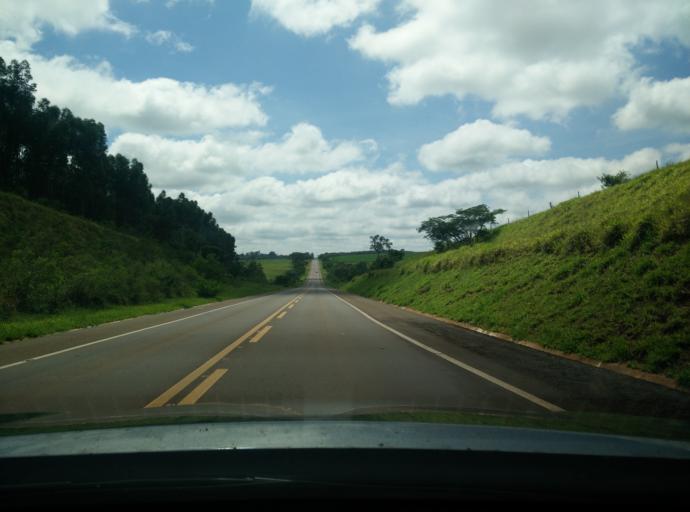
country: BR
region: Parana
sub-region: Campo Mourao
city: Campo Mourao
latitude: -23.9623
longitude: -52.5900
